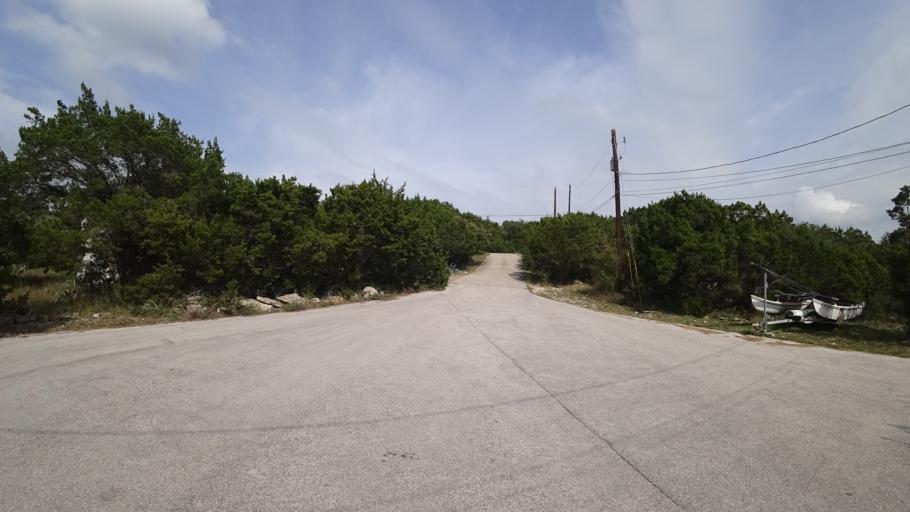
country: US
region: Texas
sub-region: Travis County
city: Hudson Bend
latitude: 30.3829
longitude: -97.9252
